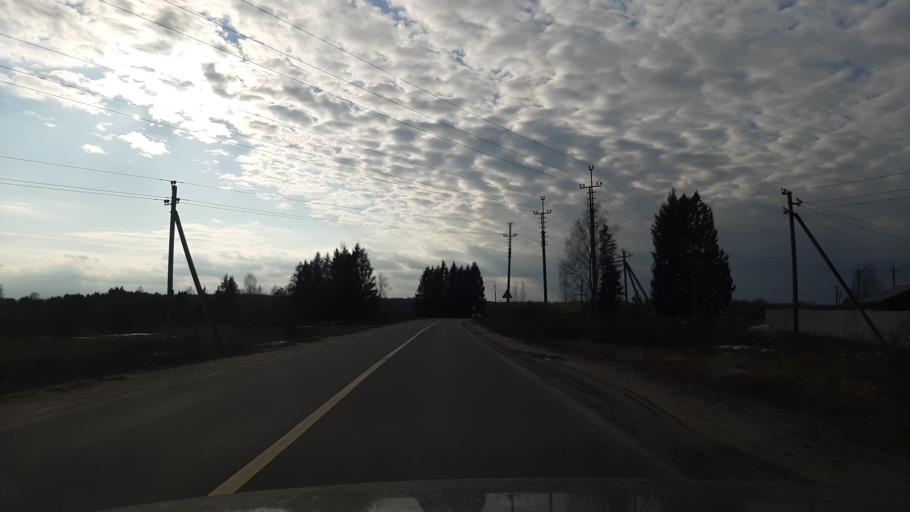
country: RU
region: Ivanovo
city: Novo-Talitsy
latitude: 56.9399
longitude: 40.7174
